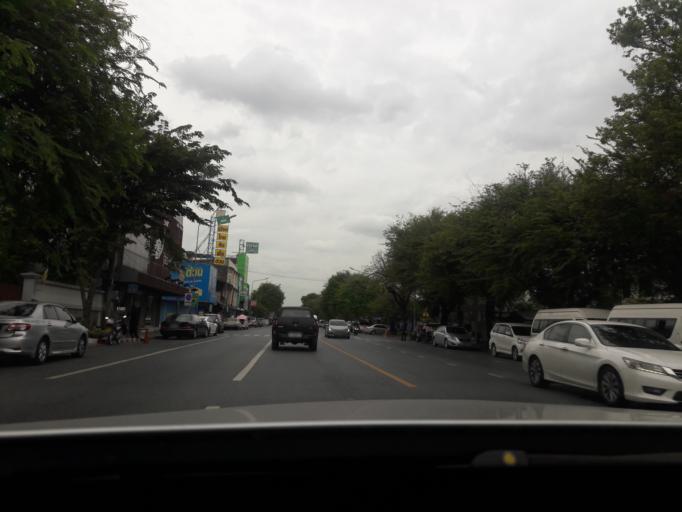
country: TH
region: Bangkok
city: Dusit
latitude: 13.7744
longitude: 100.5253
